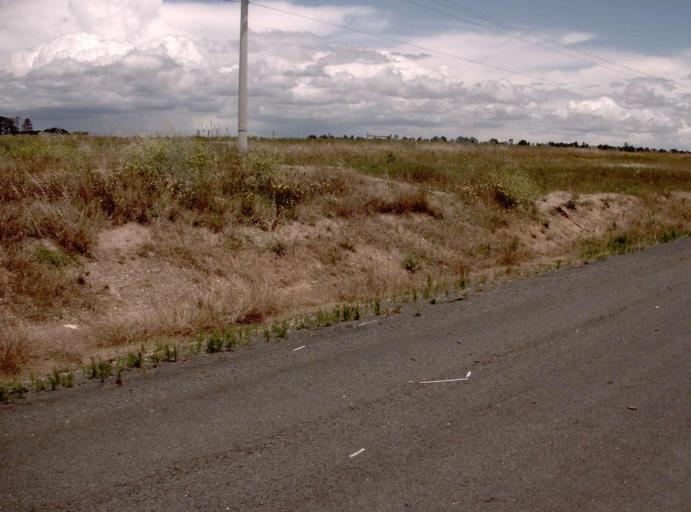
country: AU
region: Victoria
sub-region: Wellington
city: Sale
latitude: -38.1033
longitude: 147.0197
